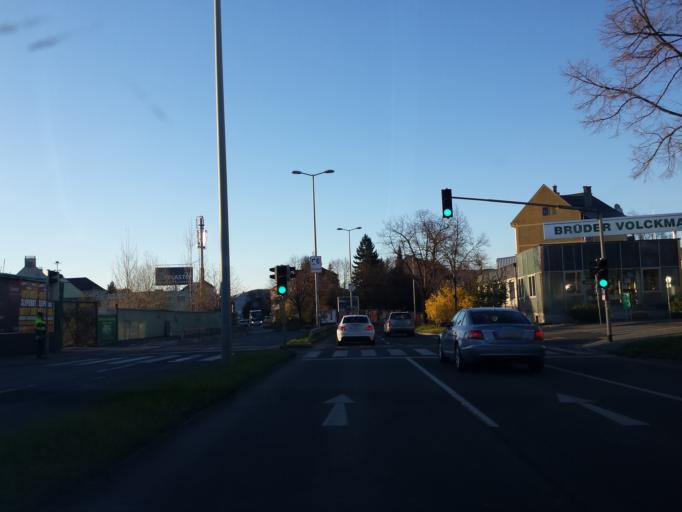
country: AT
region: Styria
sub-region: Graz Stadt
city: Goesting
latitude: 47.0802
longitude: 15.4157
